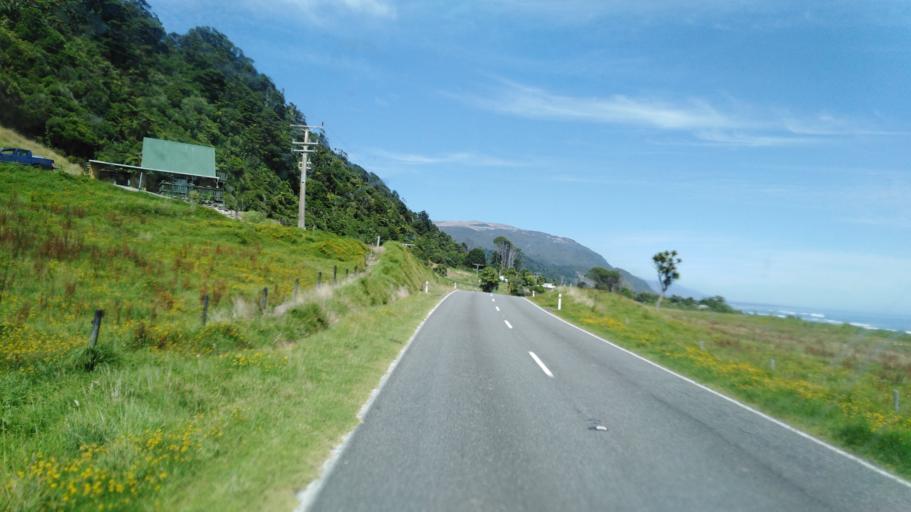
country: NZ
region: West Coast
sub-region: Buller District
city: Westport
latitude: -41.5922
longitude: 171.8898
